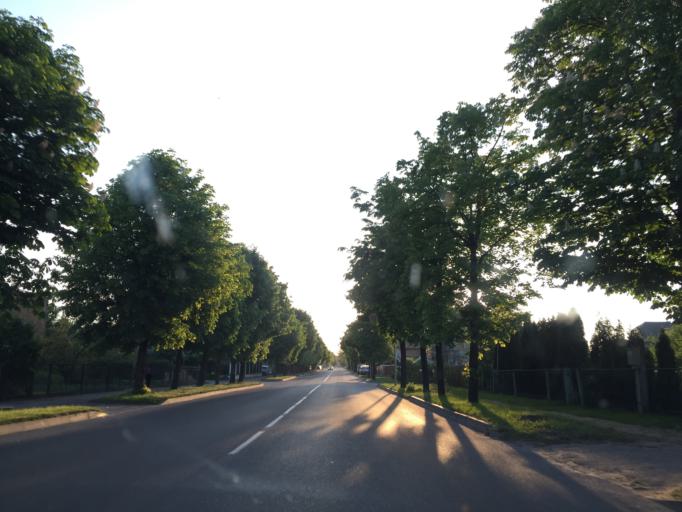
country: LT
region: Siauliu apskritis
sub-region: Siauliai
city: Siauliai
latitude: 55.9538
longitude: 23.3340
